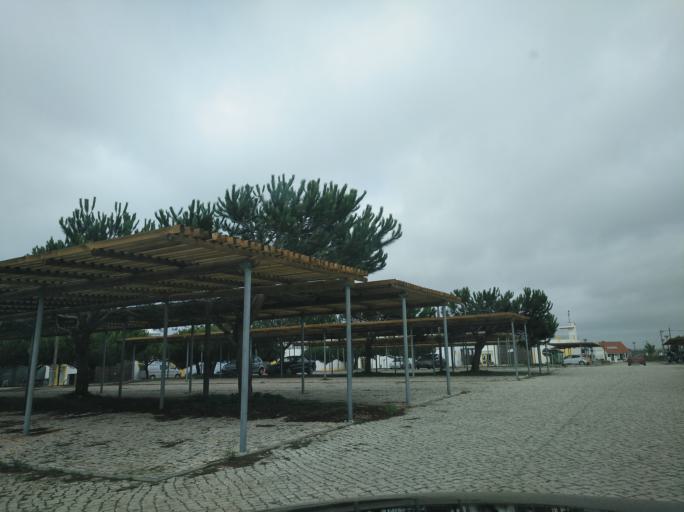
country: PT
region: Setubal
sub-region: Santiago do Cacem
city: Santo Andre
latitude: 38.1278
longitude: -8.7888
